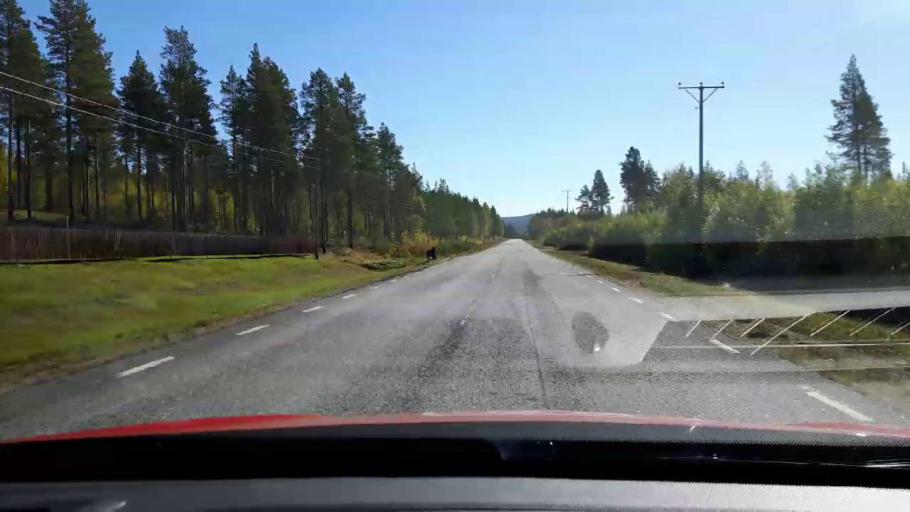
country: SE
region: Jaemtland
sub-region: Harjedalens Kommun
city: Sveg
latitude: 62.3008
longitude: 14.0639
